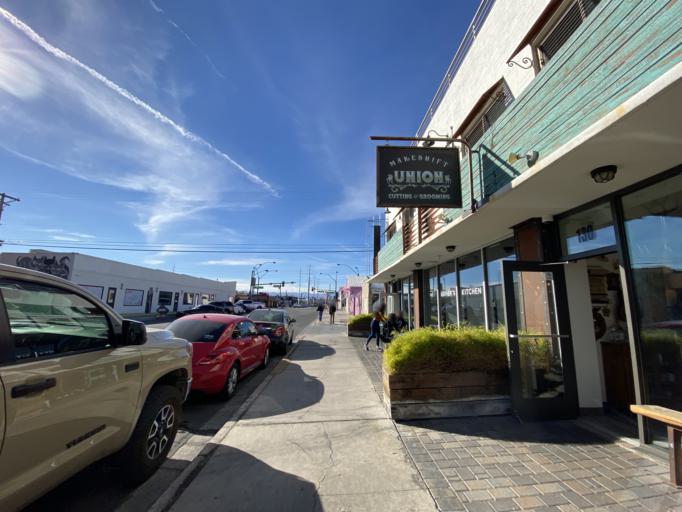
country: US
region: Nevada
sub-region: Clark County
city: Las Vegas
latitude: 36.1575
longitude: -115.1528
